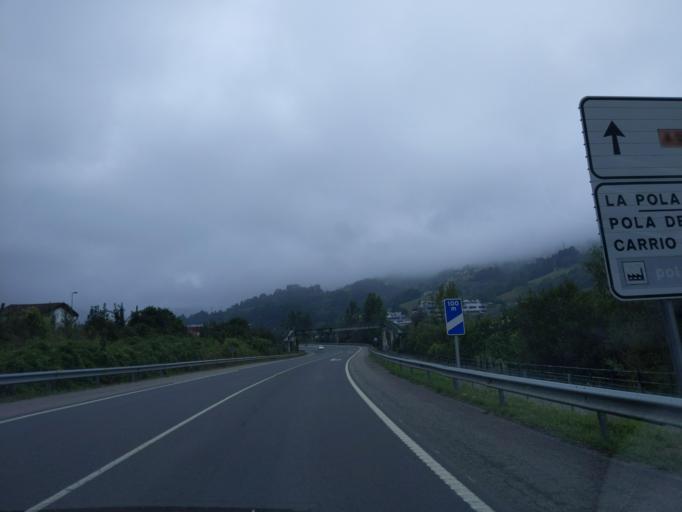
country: ES
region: Asturias
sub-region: Province of Asturias
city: Pola de Laviana
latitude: 43.2459
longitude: -5.5683
